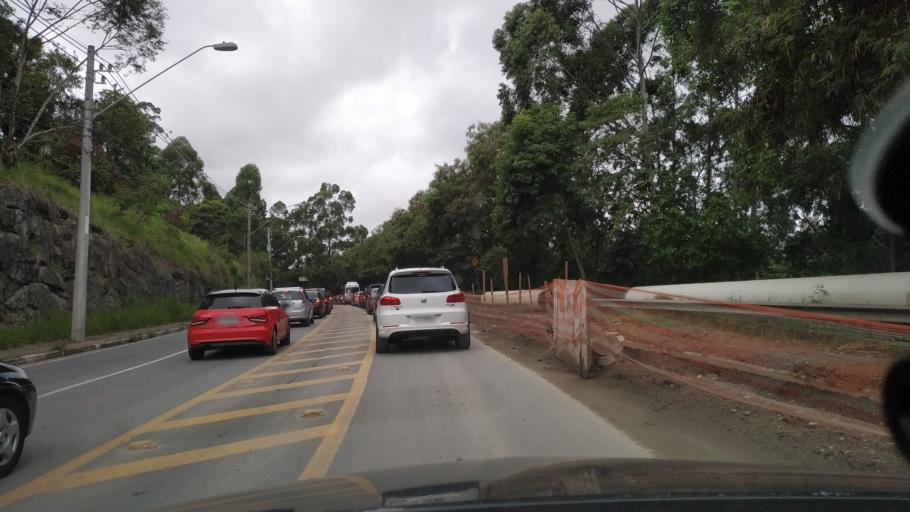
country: BR
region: Sao Paulo
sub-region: Barueri
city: Barueri
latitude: -23.4969
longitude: -46.8654
